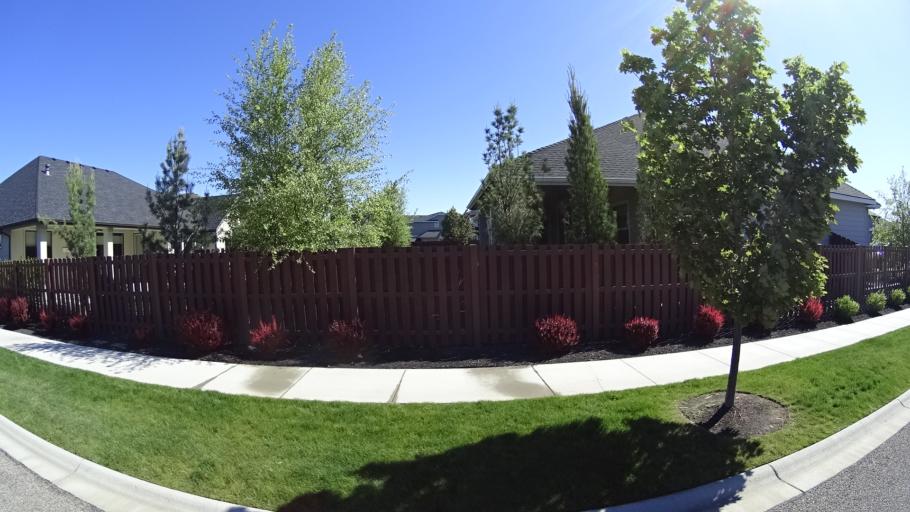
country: US
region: Idaho
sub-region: Ada County
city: Meridian
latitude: 43.6672
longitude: -116.4057
